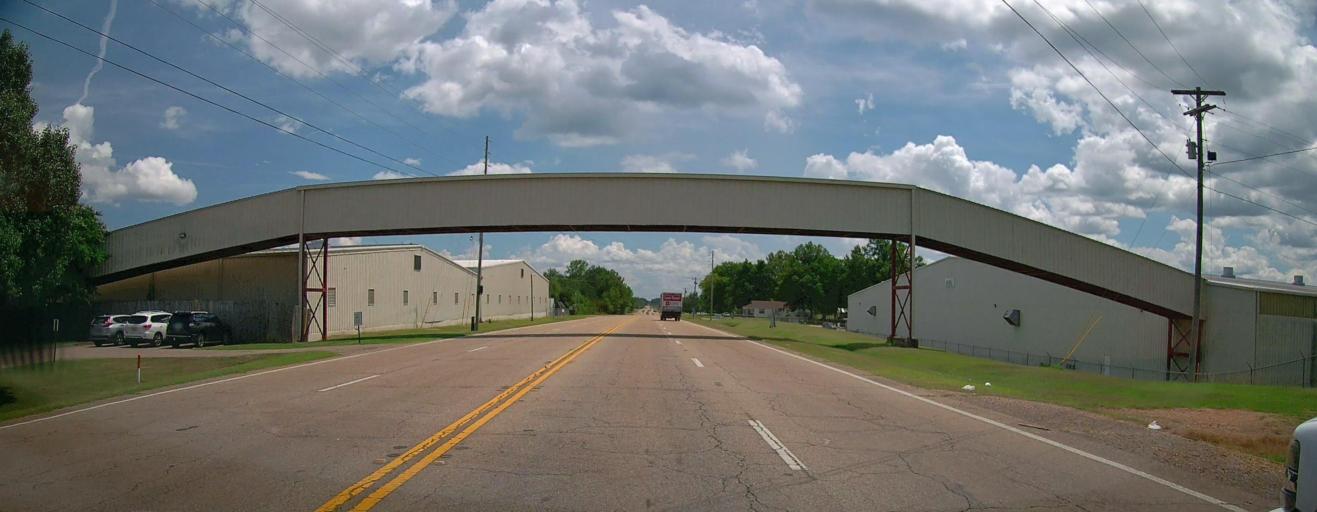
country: US
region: Mississippi
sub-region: Lee County
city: Verona
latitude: 34.1610
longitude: -88.7195
